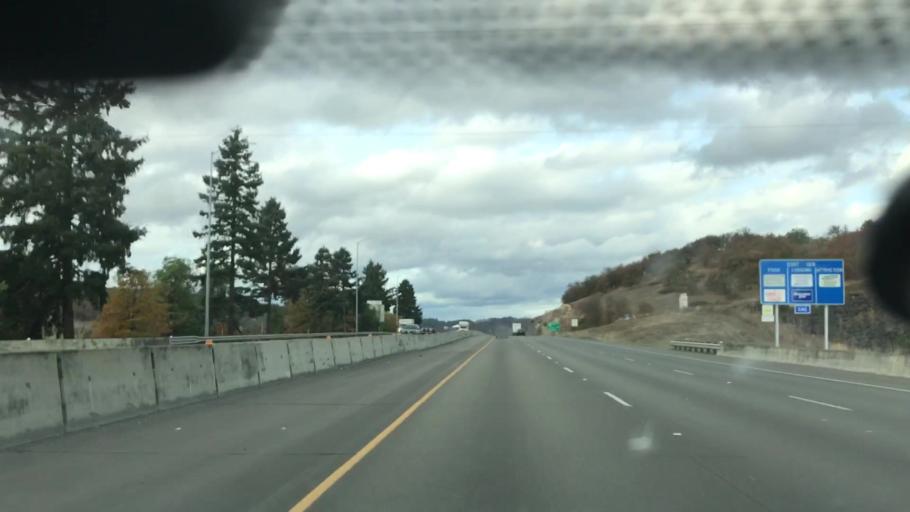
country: US
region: Oregon
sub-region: Douglas County
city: Green
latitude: 43.1604
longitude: -123.3653
